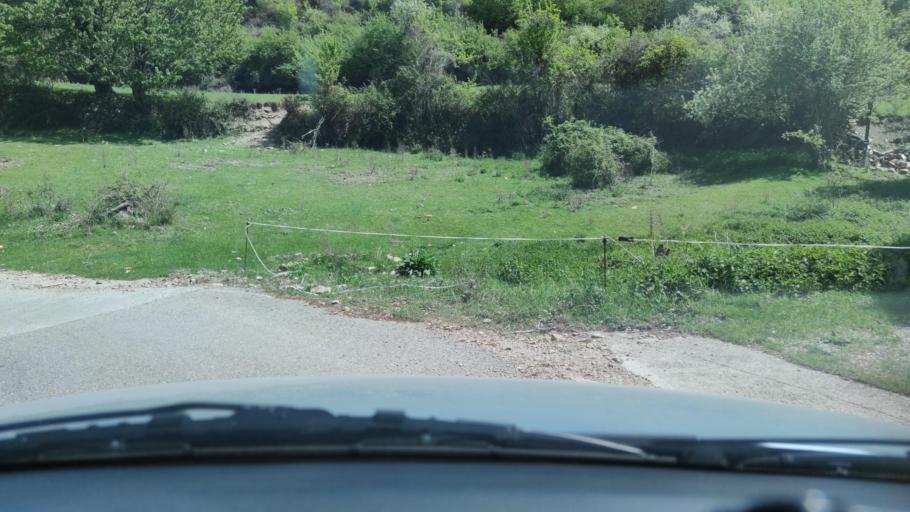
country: ES
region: Catalonia
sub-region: Provincia de Lleida
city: Sort
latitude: 42.3242
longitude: 1.1068
